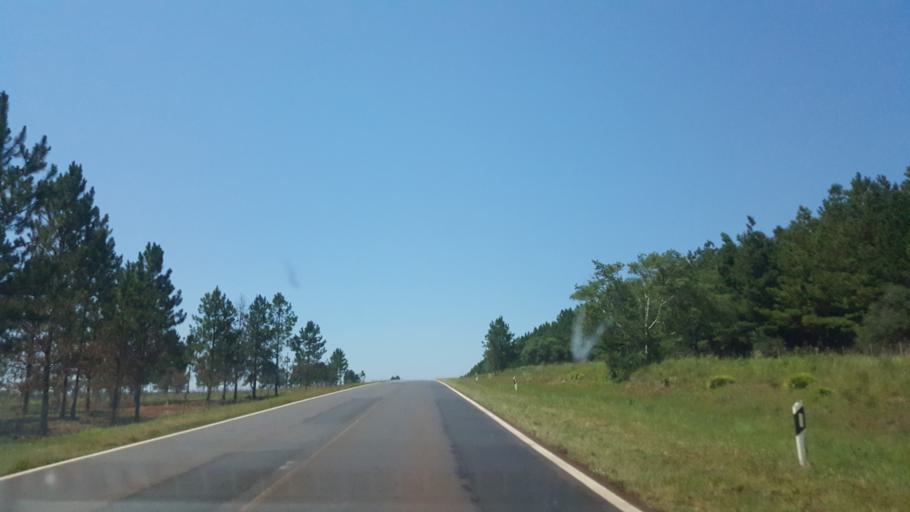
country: AR
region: Corrientes
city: Santo Tome
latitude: -28.3883
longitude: -56.1076
